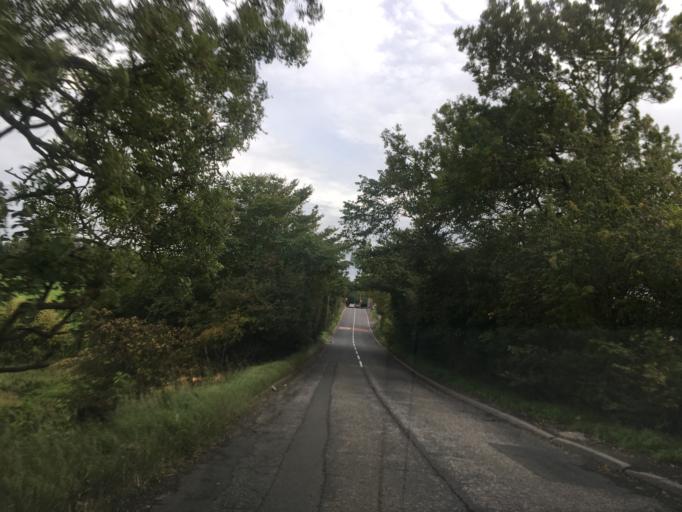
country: GB
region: Scotland
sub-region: West Lothian
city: Kirknewton
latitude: 55.9035
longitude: -3.4067
